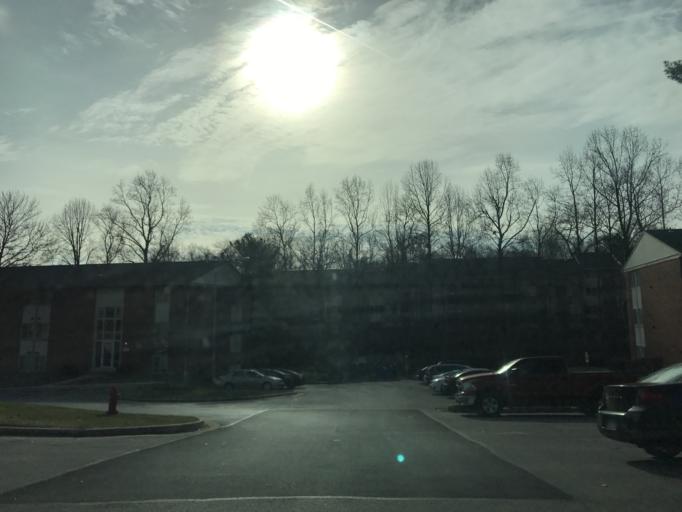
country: US
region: Maryland
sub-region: Baltimore County
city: Carney
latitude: 39.4010
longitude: -76.5215
